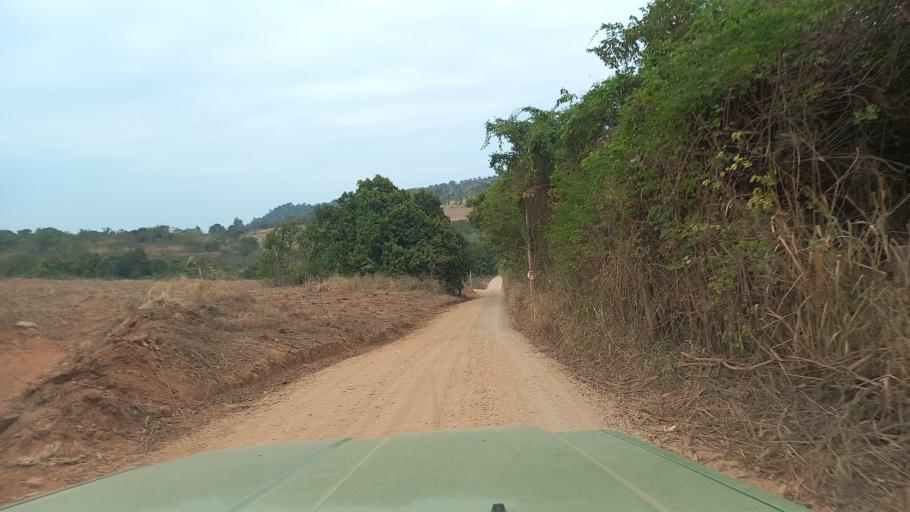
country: BR
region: Sao Paulo
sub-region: Moji-Guacu
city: Mogi-Gaucu
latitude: -22.2809
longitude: -46.8454
